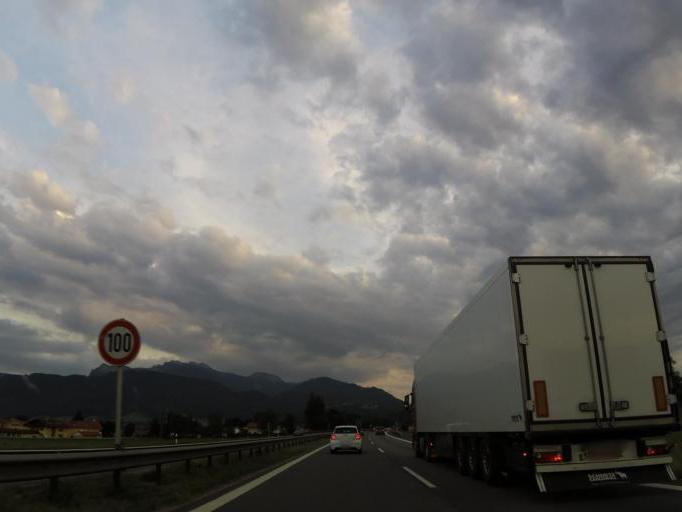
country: DE
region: Bavaria
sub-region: Upper Bavaria
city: Bernau am Chiemsee
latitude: 47.8250
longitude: 12.3827
